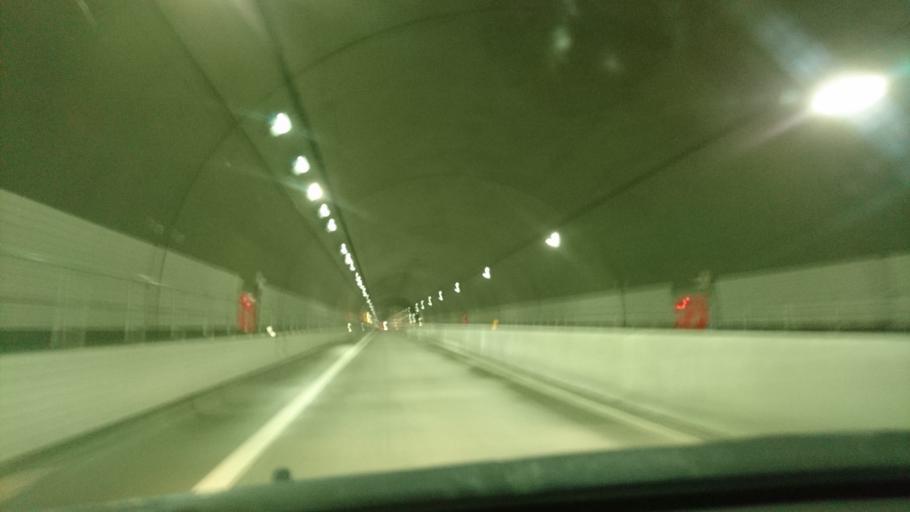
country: JP
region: Iwate
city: Kamaishi
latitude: 39.1860
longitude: 141.8506
